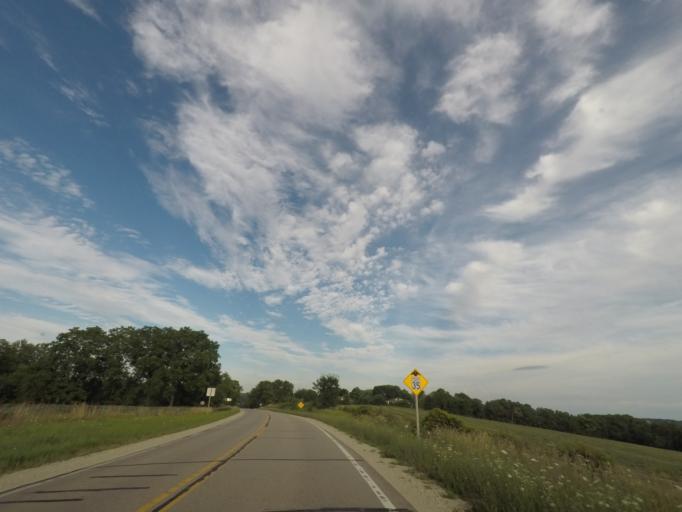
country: US
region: Wisconsin
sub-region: Green County
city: New Glarus
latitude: 42.8144
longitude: -89.6504
